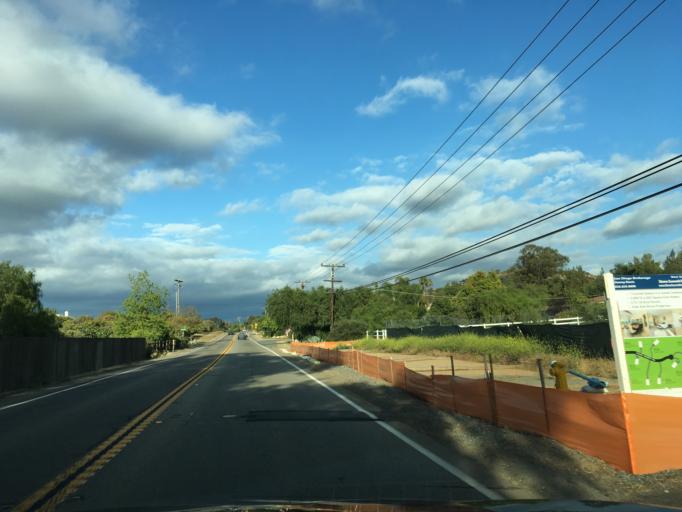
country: US
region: California
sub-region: San Diego County
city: Hidden Meadows
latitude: 33.2563
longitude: -117.0818
